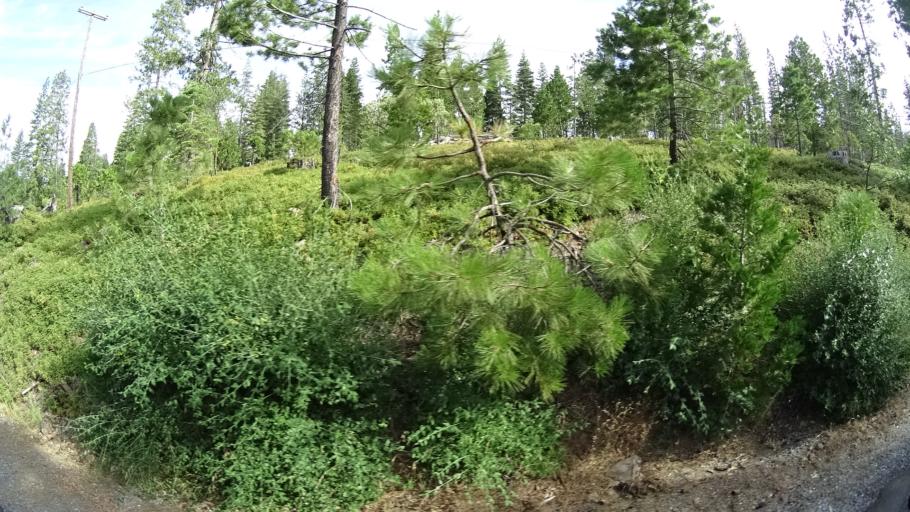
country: US
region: California
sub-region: Calaveras County
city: Arnold
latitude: 38.2665
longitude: -120.3223
